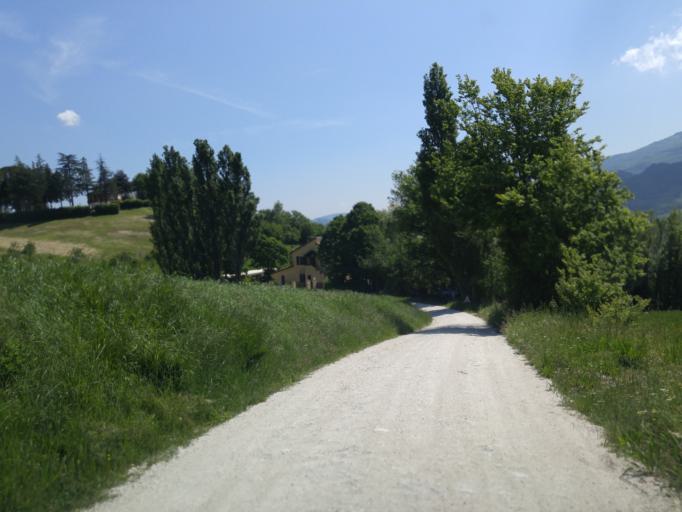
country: IT
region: The Marches
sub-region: Provincia di Pesaro e Urbino
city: Fermignano
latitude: 43.6999
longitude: 12.6486
